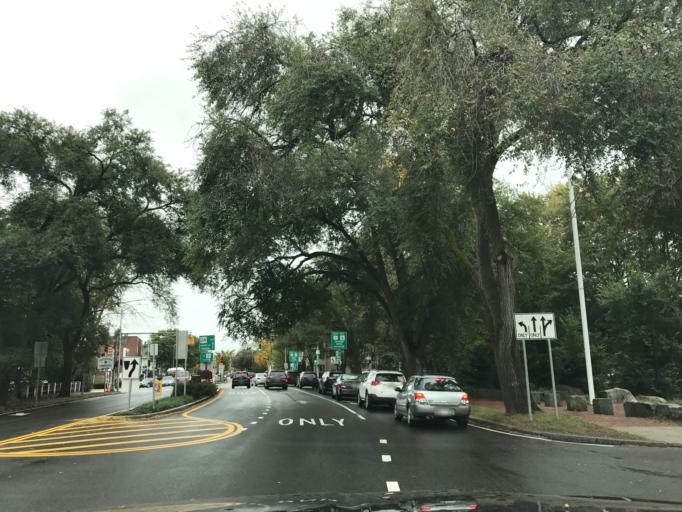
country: US
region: Massachusetts
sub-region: Middlesex County
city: Arlington
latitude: 42.4014
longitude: -71.1369
